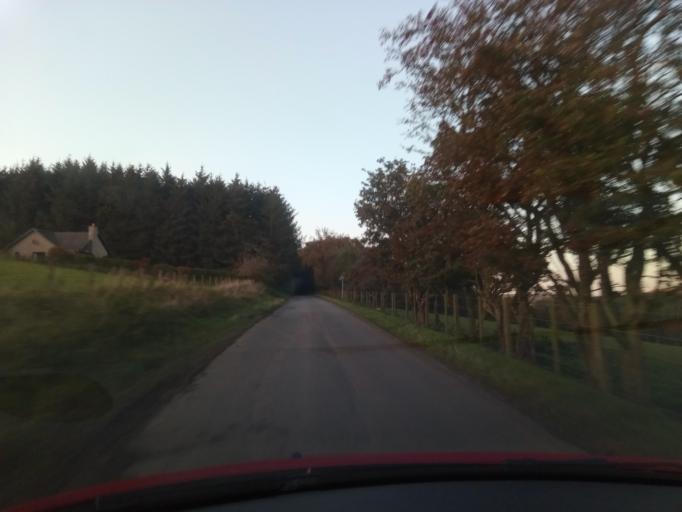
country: GB
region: Scotland
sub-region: Fife
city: Pathhead
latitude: 55.7935
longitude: -2.8897
